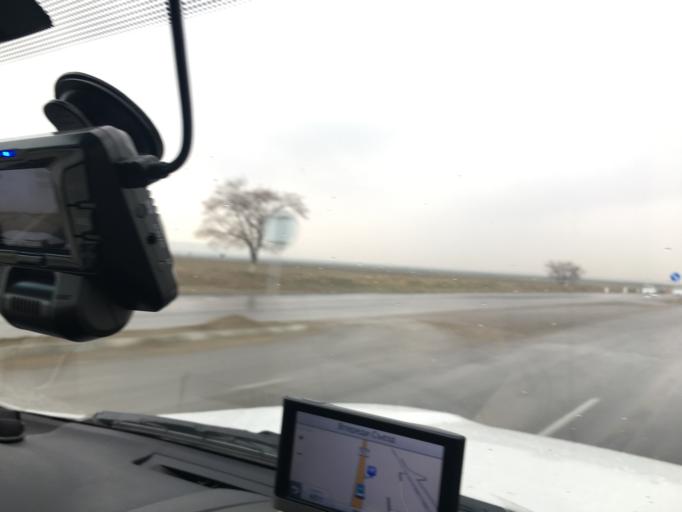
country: TM
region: Ahal
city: Annau
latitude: 37.8294
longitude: 58.7468
